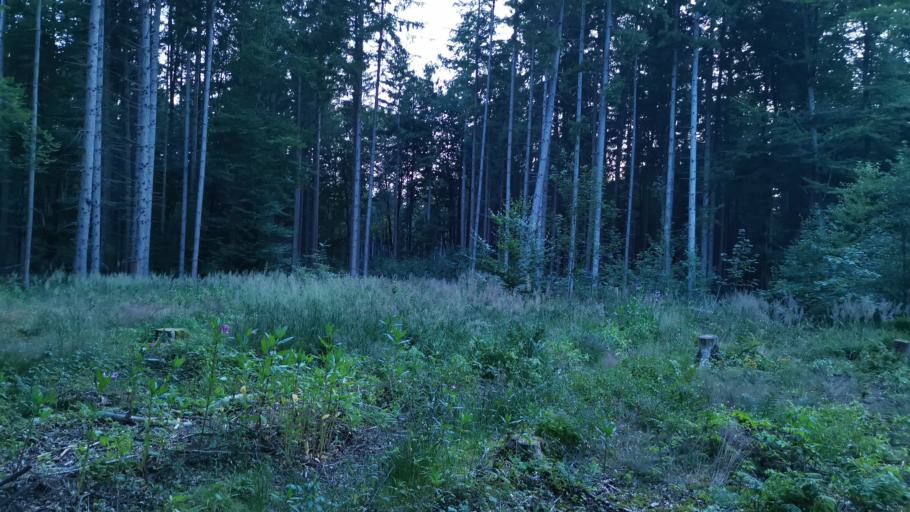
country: DE
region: Bavaria
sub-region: Upper Bavaria
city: Neuried
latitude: 48.0687
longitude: 11.4762
